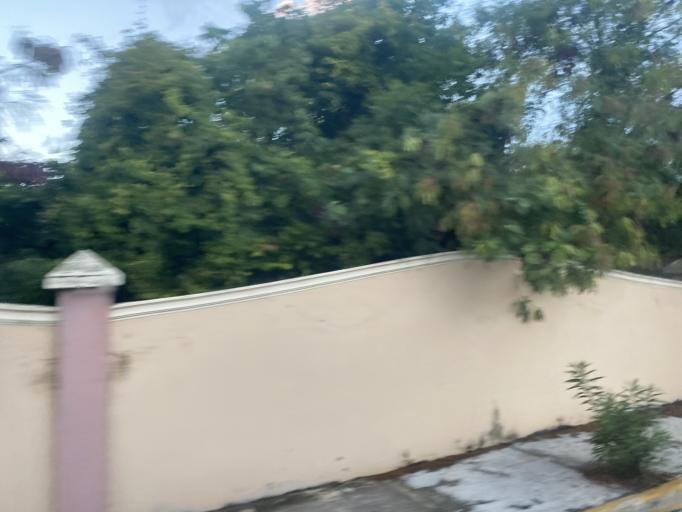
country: DO
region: San Juan
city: Punta Cana
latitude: 18.7126
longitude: -68.4594
